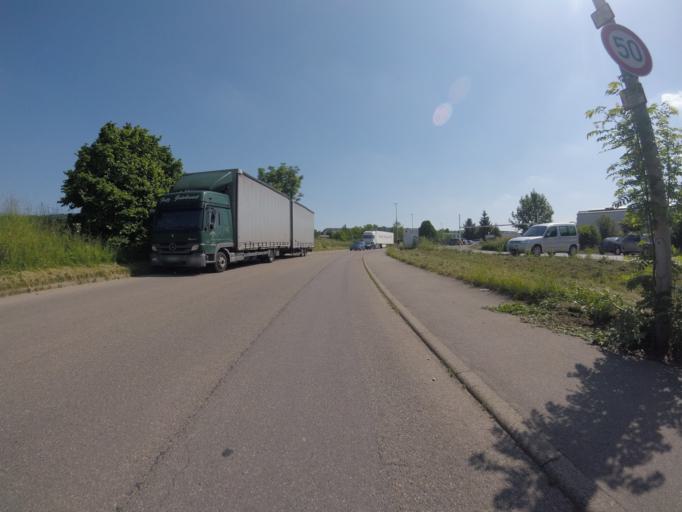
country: DE
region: Baden-Wuerttemberg
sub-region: Regierungsbezirk Stuttgart
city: Grossbottwar
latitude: 49.0041
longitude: 9.3038
